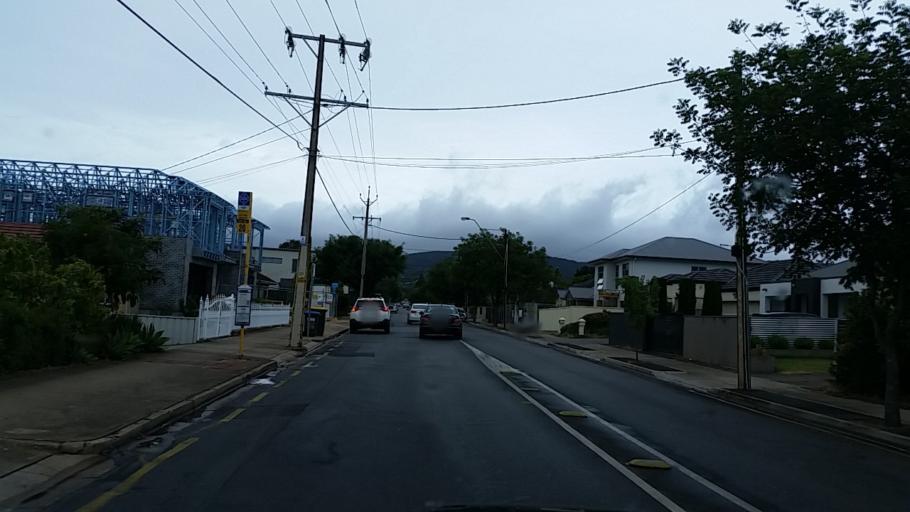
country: AU
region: South Australia
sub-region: Campbelltown
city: Hectorville
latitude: -34.8970
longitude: 138.6661
